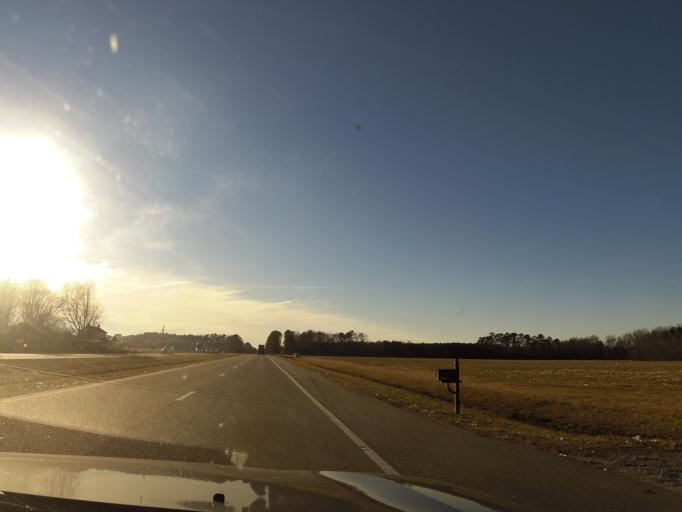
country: US
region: Virginia
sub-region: City of Franklin
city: Franklin
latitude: 36.6542
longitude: -76.8258
